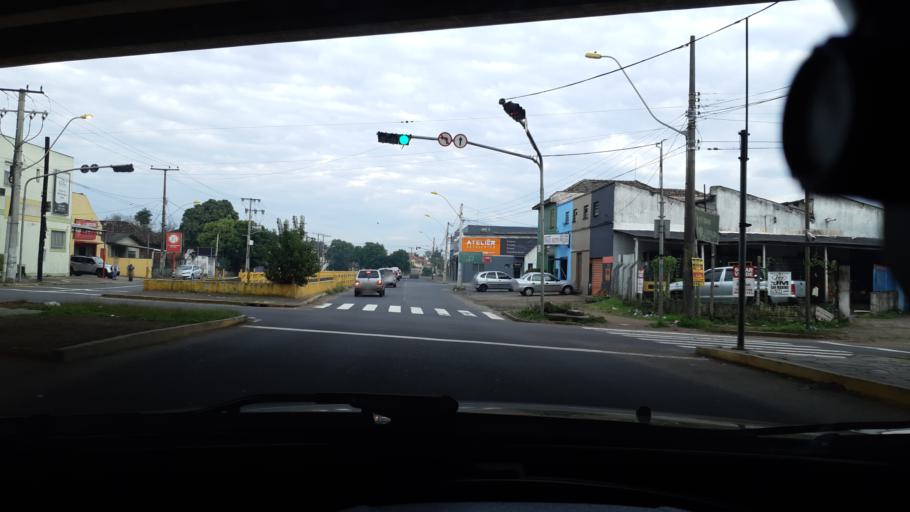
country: BR
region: Rio Grande do Sul
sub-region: Sao Leopoldo
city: Sao Leopoldo
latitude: -29.7723
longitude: -51.1541
